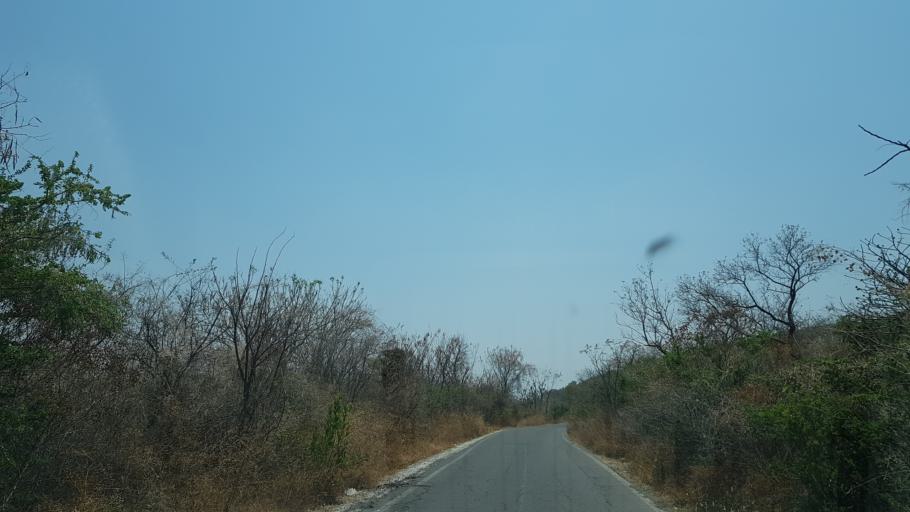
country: MX
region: Puebla
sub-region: Atzitzihuacan
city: San Miguel Aguacomulican
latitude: 18.7970
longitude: -98.5464
